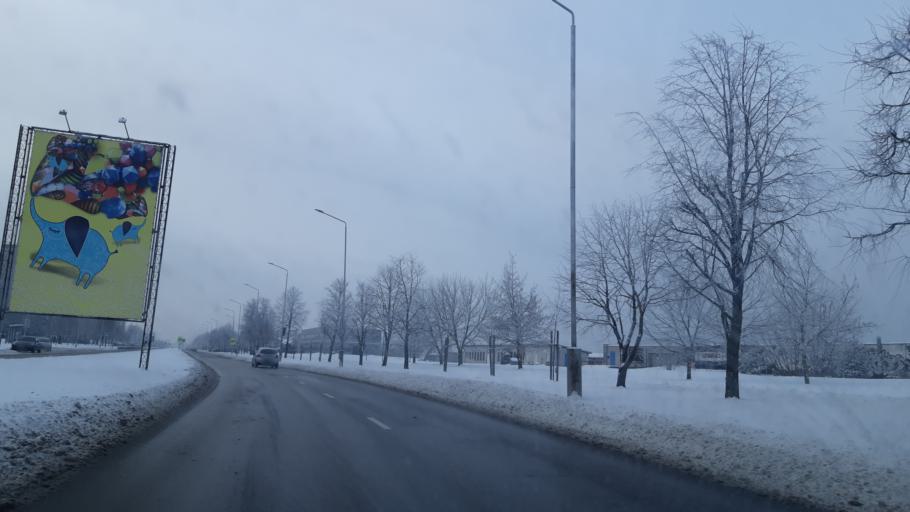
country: LT
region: Kauno apskritis
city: Dainava (Kaunas)
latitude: 54.9307
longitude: 23.9672
